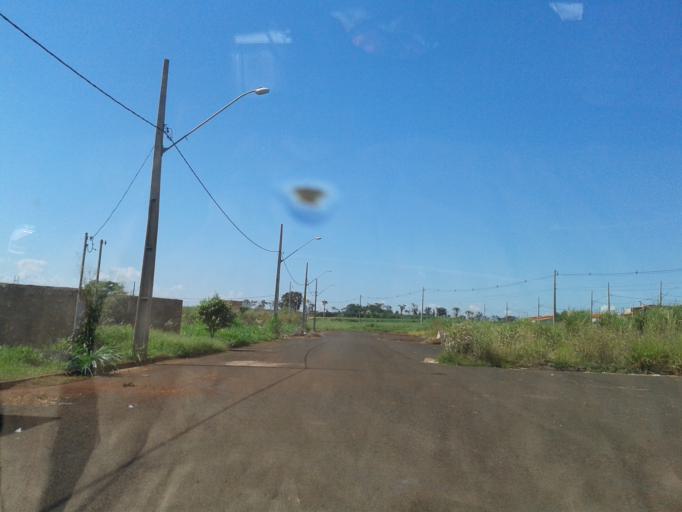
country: BR
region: Goias
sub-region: Itumbiara
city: Itumbiara
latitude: -18.4264
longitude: -49.1838
